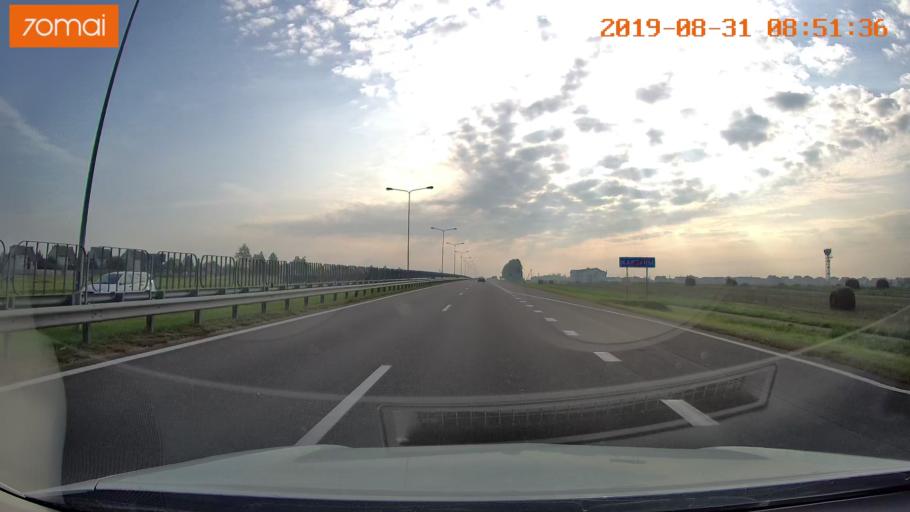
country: BY
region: Minsk
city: Smilavichy
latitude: 53.7597
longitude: 27.9840
